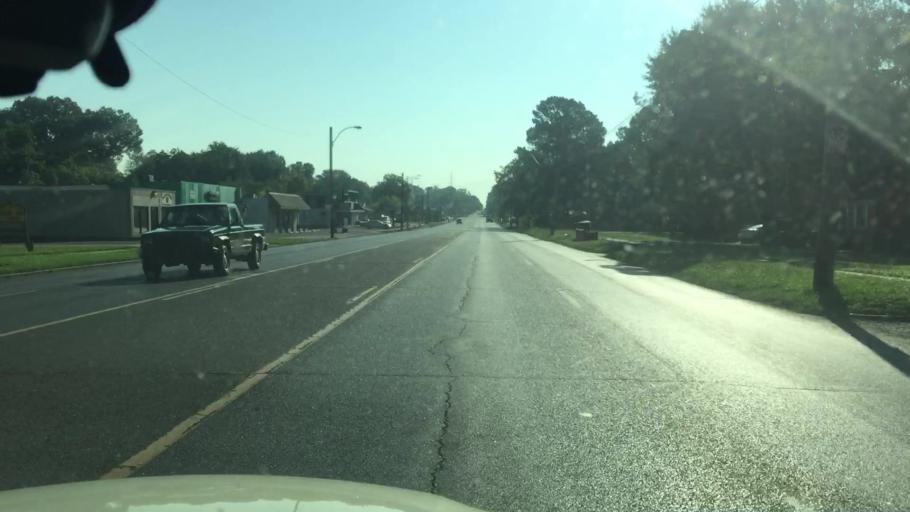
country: US
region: Tennessee
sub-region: Shelby County
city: Bartlett
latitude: 35.1076
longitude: -89.9369
